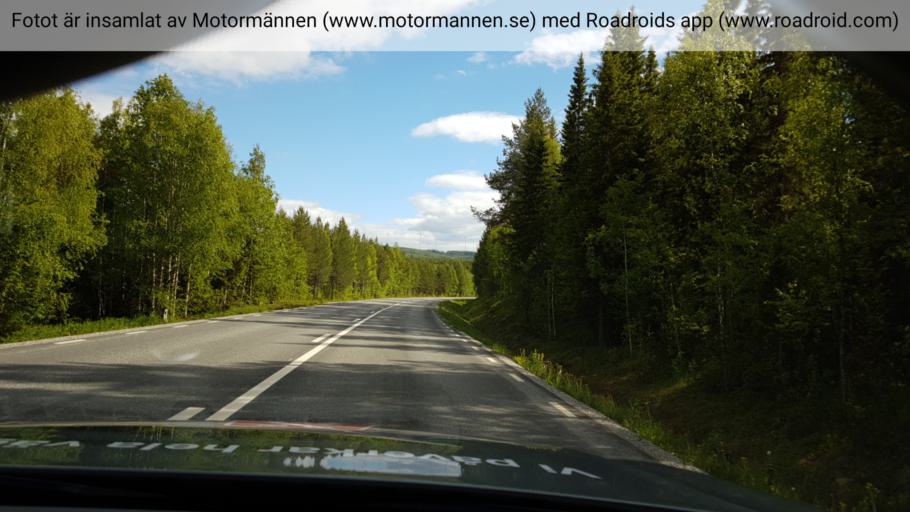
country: SE
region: Jaemtland
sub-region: Stroemsunds Kommun
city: Stroemsund
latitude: 64.1489
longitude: 15.6821
